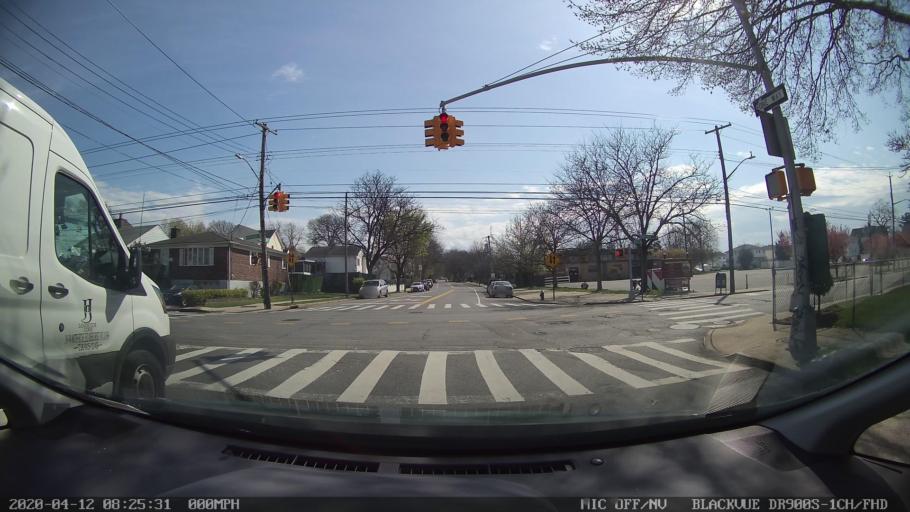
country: US
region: New York
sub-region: Richmond County
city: Bloomfield
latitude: 40.6164
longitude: -74.1398
